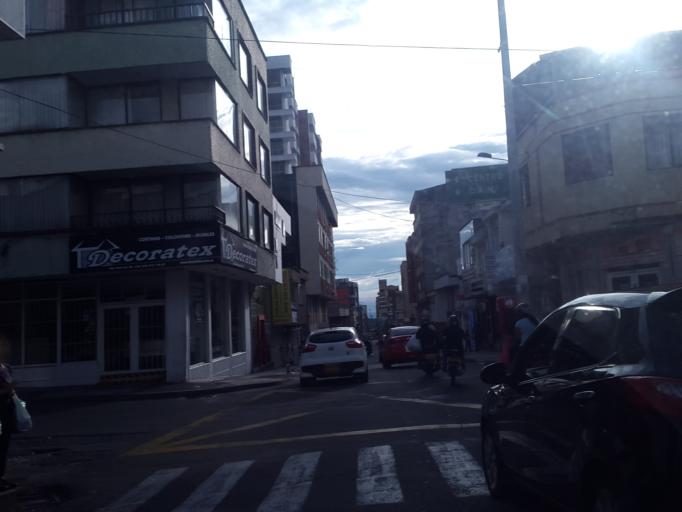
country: CO
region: Quindio
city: Armenia
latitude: 4.5371
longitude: -75.6694
